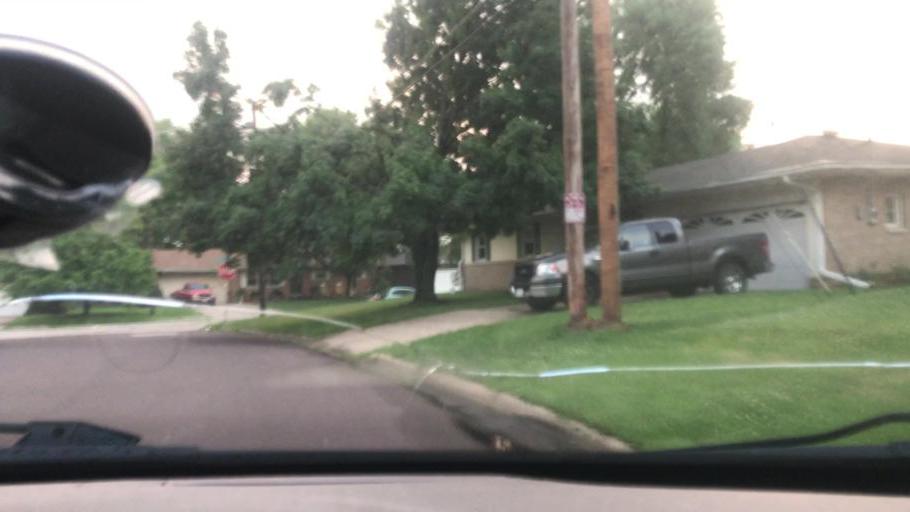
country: US
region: Illinois
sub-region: Tazewell County
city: Pekin
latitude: 40.5499
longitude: -89.6130
